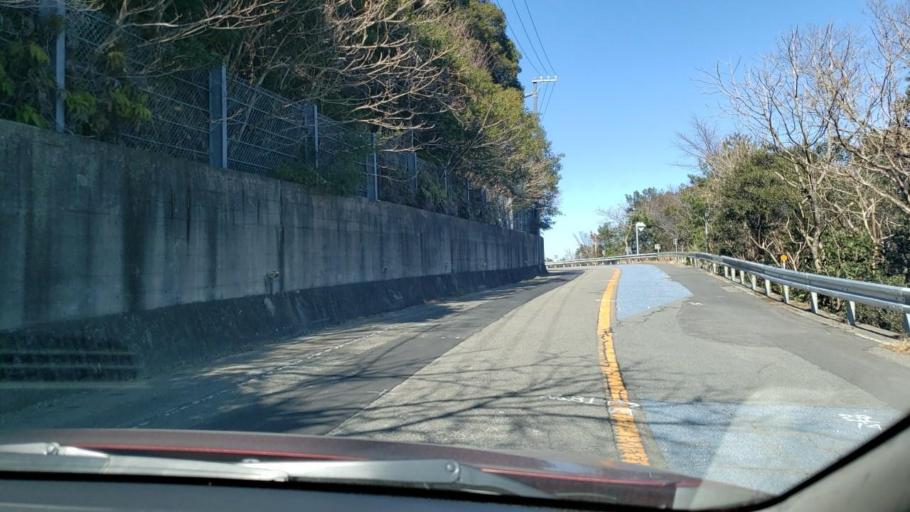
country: JP
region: Tokushima
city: Narutocho-mitsuishi
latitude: 34.2350
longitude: 134.6153
